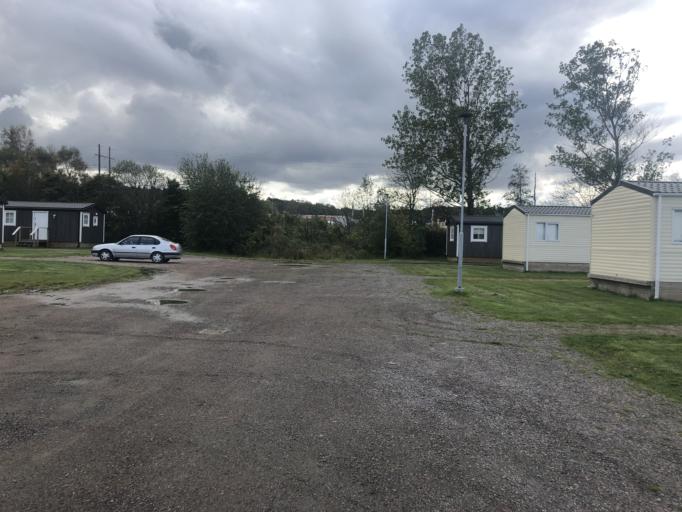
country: SE
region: Vaestra Goetaland
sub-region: Molndal
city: Moelndal
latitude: 57.6454
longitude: 11.9932
